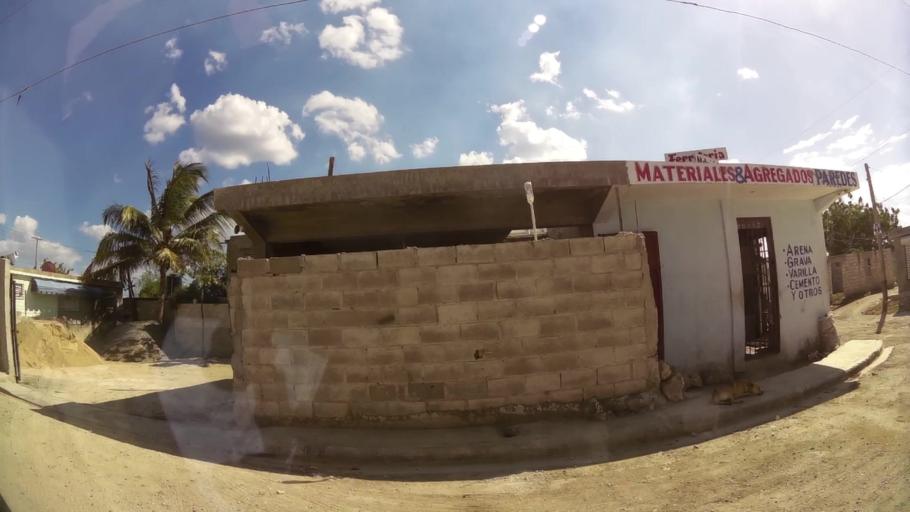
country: DO
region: Santo Domingo
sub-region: Santo Domingo
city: Santo Domingo Este
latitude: 18.4729
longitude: -69.7666
